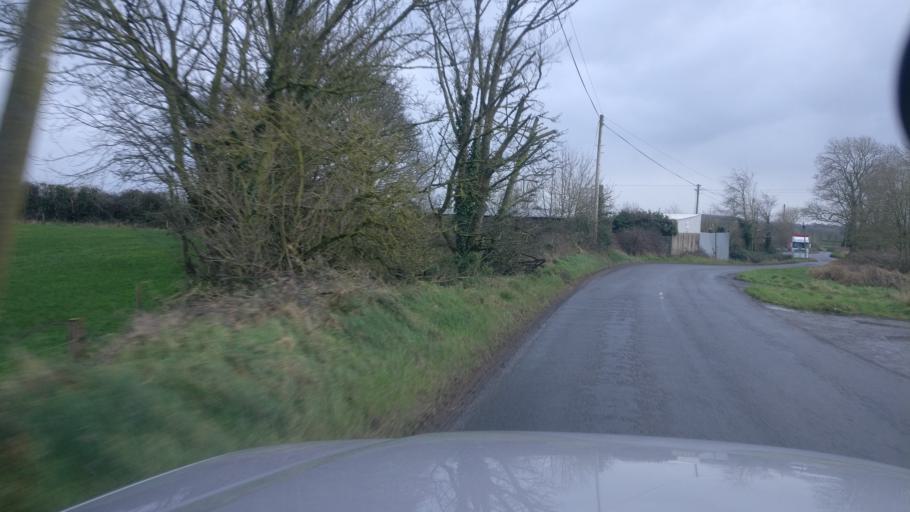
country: IE
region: Munster
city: Nenagh Bridge
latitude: 52.9879
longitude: -8.1142
